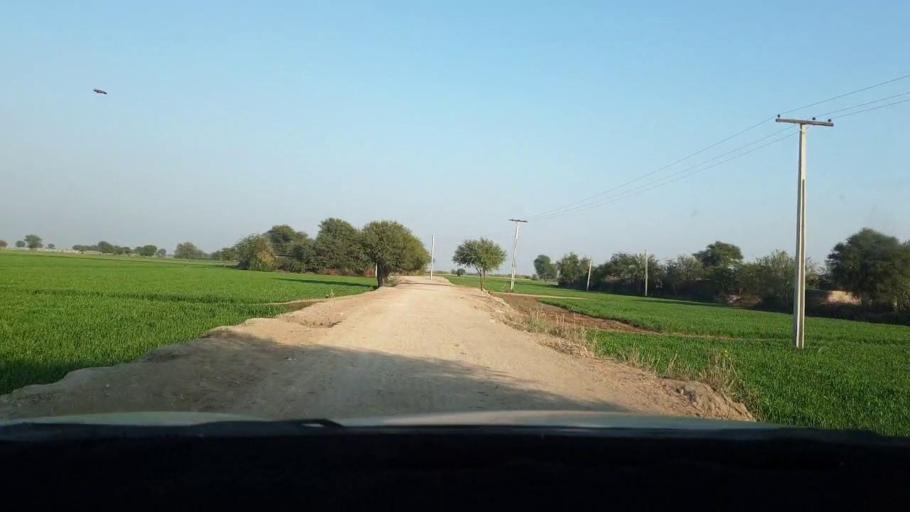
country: PK
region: Sindh
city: Berani
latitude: 25.7460
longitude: 68.7427
